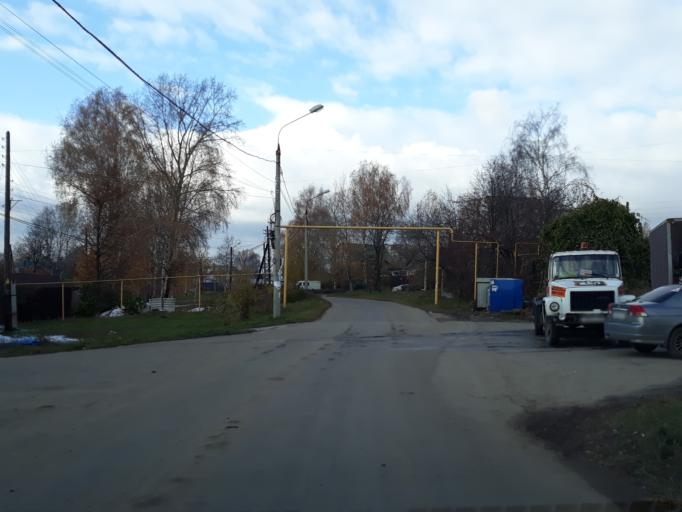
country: RU
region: Nizjnij Novgorod
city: Afonino
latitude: 56.2315
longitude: 44.0092
